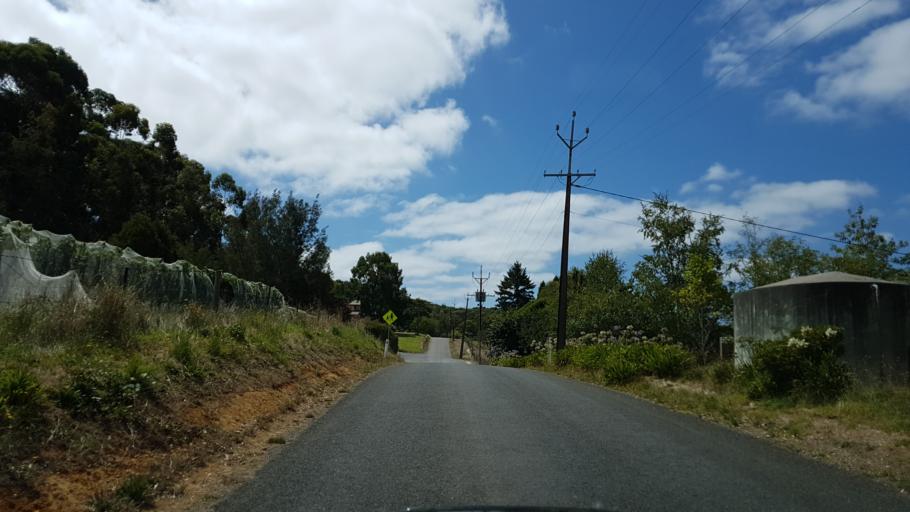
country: AU
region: South Australia
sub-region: Adelaide Hills
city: Crafers
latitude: -34.9778
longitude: 138.7171
